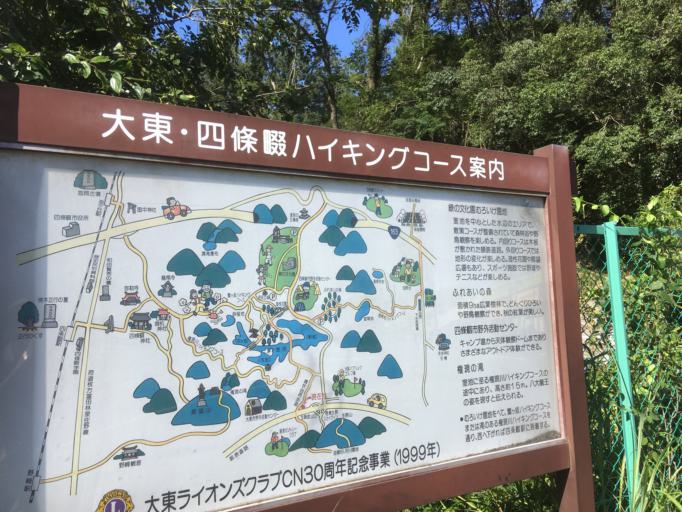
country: JP
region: Nara
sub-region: Ikoma-shi
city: Ikoma
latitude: 34.7161
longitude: 135.6701
